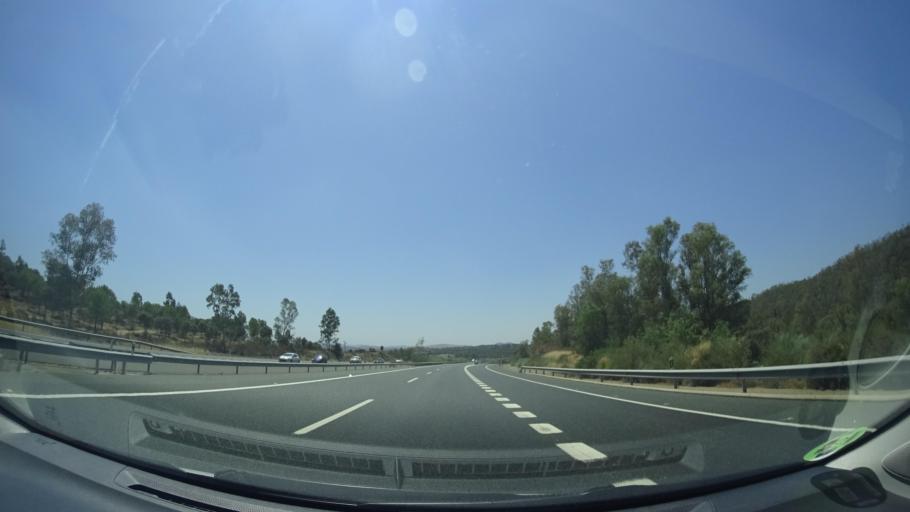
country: ES
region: Extremadura
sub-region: Provincia de Badajoz
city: Monesterio
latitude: 38.0339
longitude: -6.2233
